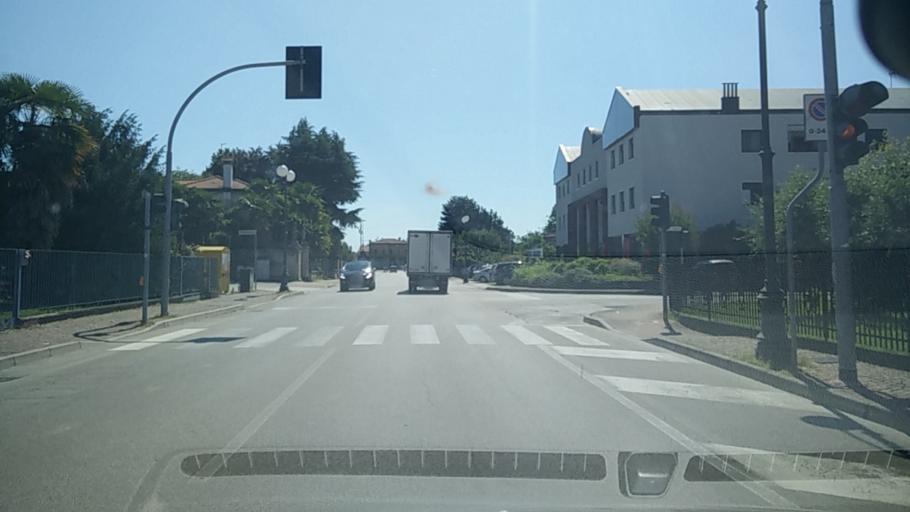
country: IT
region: Veneto
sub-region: Provincia di Venezia
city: Camponogara
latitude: 45.3828
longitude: 12.0759
